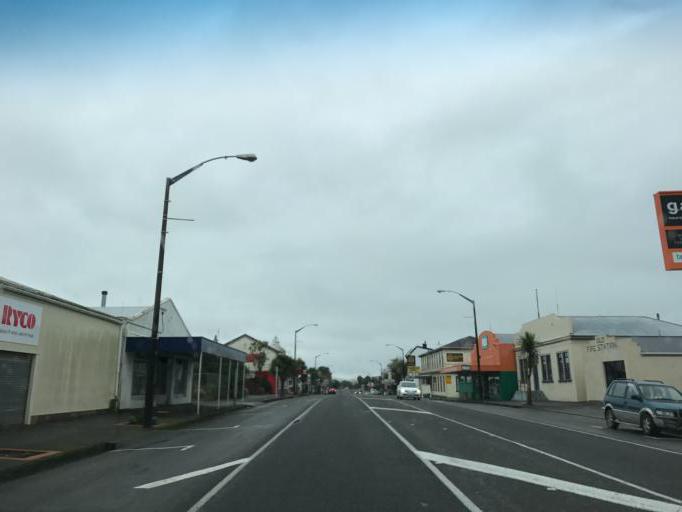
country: NZ
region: Taranaki
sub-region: South Taranaki District
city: Patea
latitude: -39.7642
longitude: 174.6316
